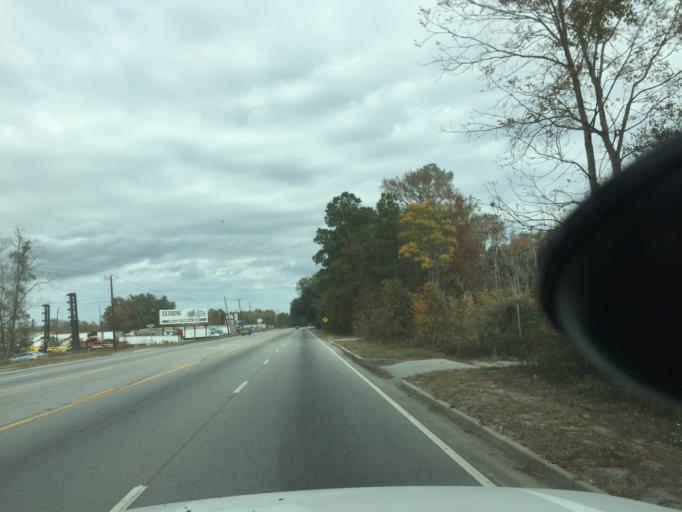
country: US
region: Georgia
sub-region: Chatham County
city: Garden City
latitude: 32.1055
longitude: -81.1957
